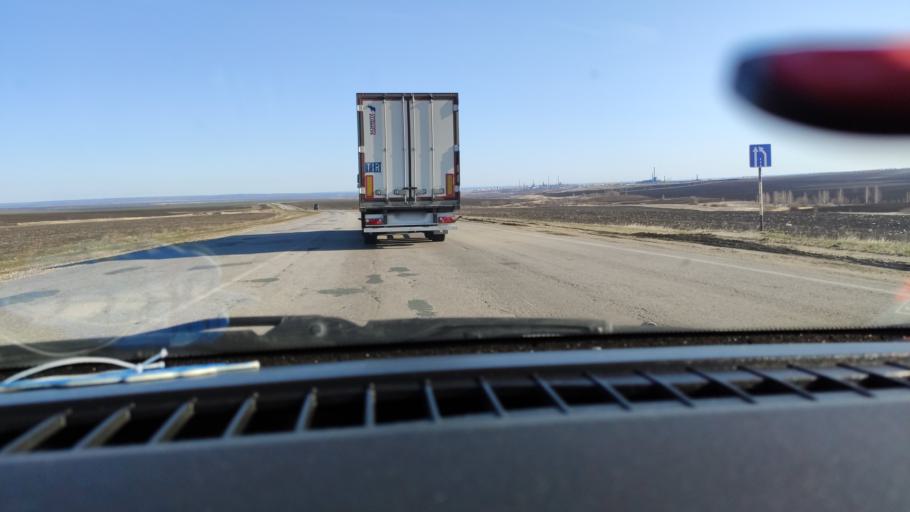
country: RU
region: Samara
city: Syzran'
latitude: 53.0049
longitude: 48.3314
